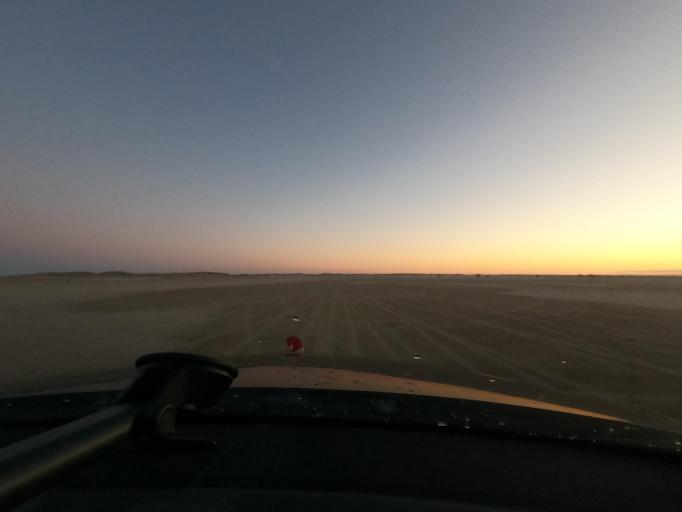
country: DE
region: Schleswig-Holstein
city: List
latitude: 55.1537
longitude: 8.4799
